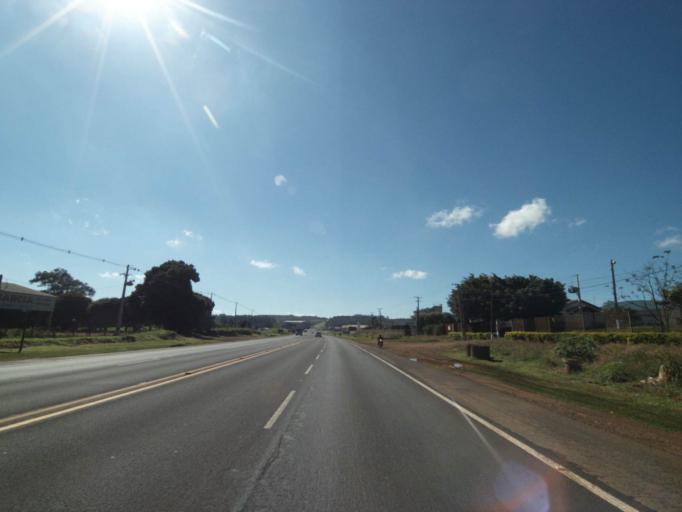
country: BR
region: Parana
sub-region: Arapongas
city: Arapongas
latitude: -23.4001
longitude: -51.4634
